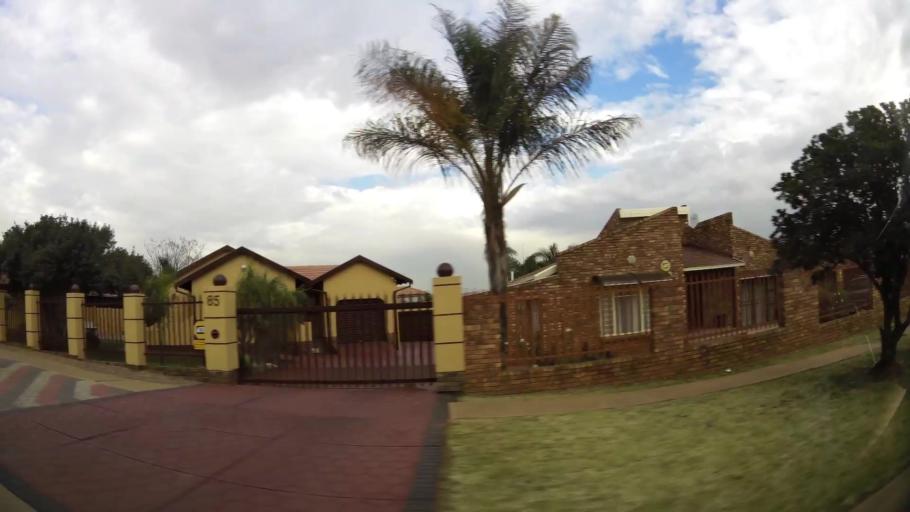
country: ZA
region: Gauteng
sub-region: City of Tshwane Metropolitan Municipality
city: Pretoria
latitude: -25.6984
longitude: 28.3029
